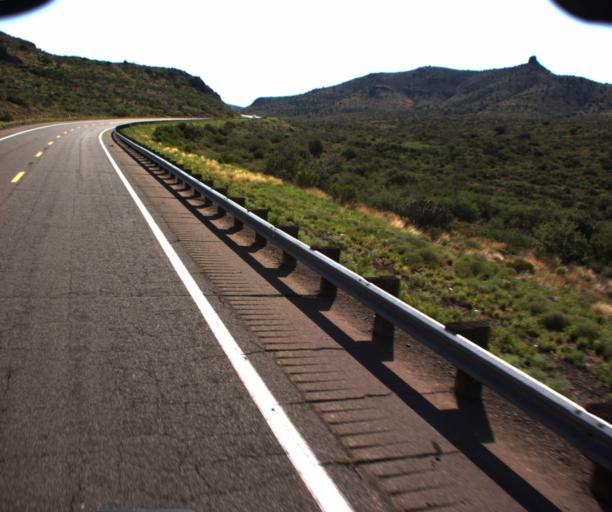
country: US
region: Arizona
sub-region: Greenlee County
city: Clifton
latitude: 32.8476
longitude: -109.3513
